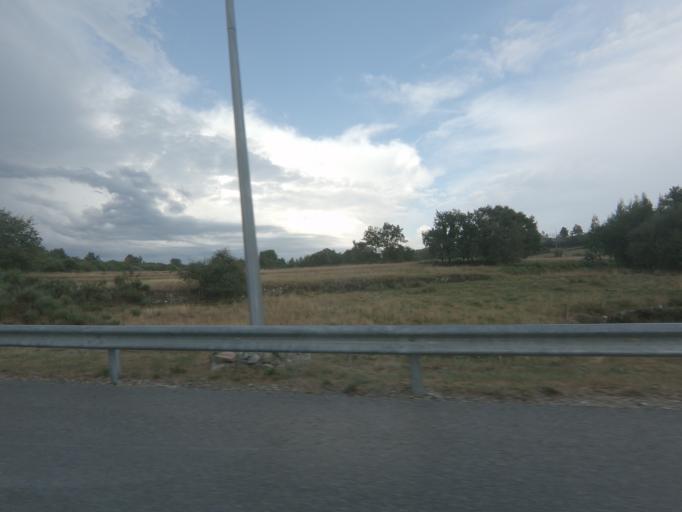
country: PT
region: Viseu
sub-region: Castro Daire
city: Castro Daire
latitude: 40.9626
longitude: -7.8904
